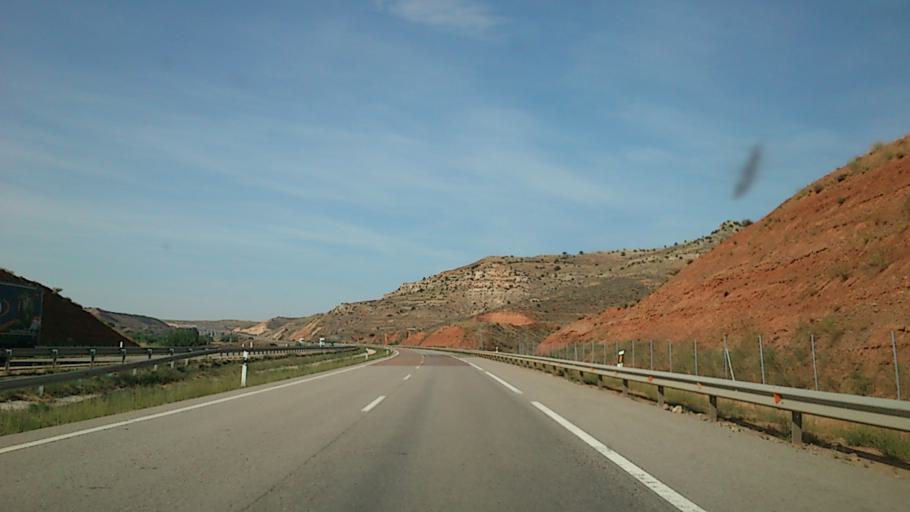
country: ES
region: Aragon
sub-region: Provincia de Teruel
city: Calamocha
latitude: 40.9657
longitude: -1.2614
